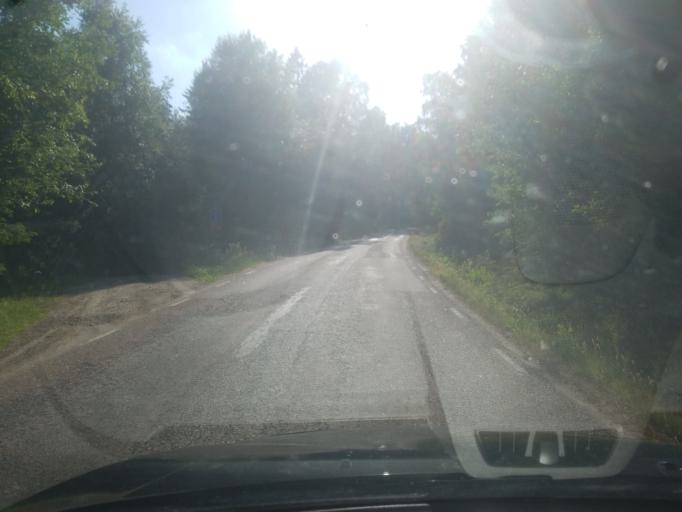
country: SE
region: Vaestra Goetaland
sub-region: Orust
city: Henan
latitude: 58.2912
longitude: 11.6464
